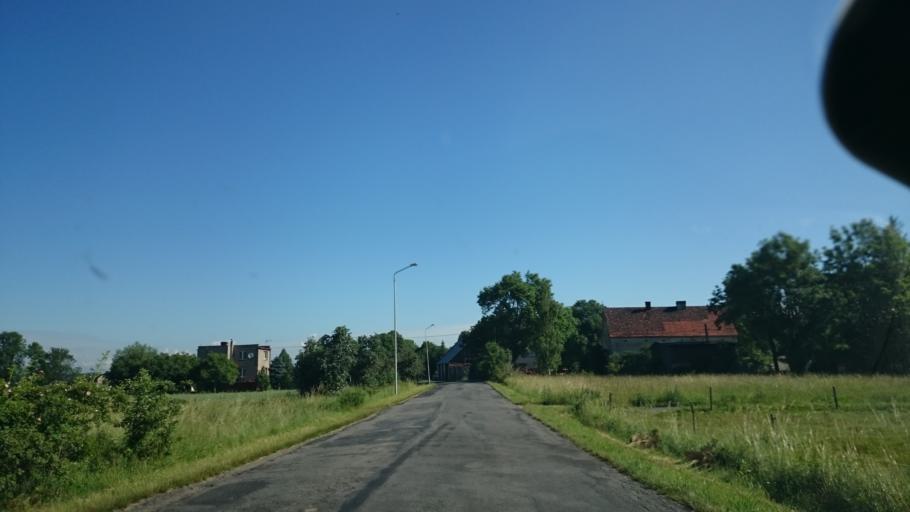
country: PL
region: Lower Silesian Voivodeship
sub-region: Powiat klodzki
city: Bystrzyca Klodzka
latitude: 50.2626
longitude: 16.6414
